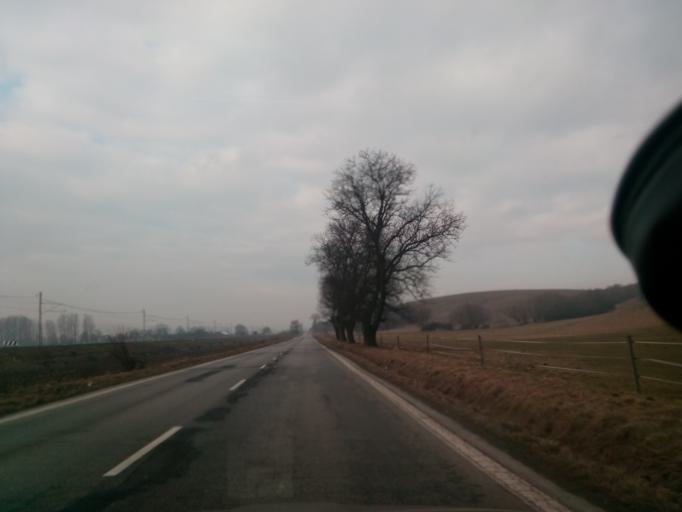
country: SK
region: Presovsky
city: Lipany
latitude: 49.1413
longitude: 21.0033
